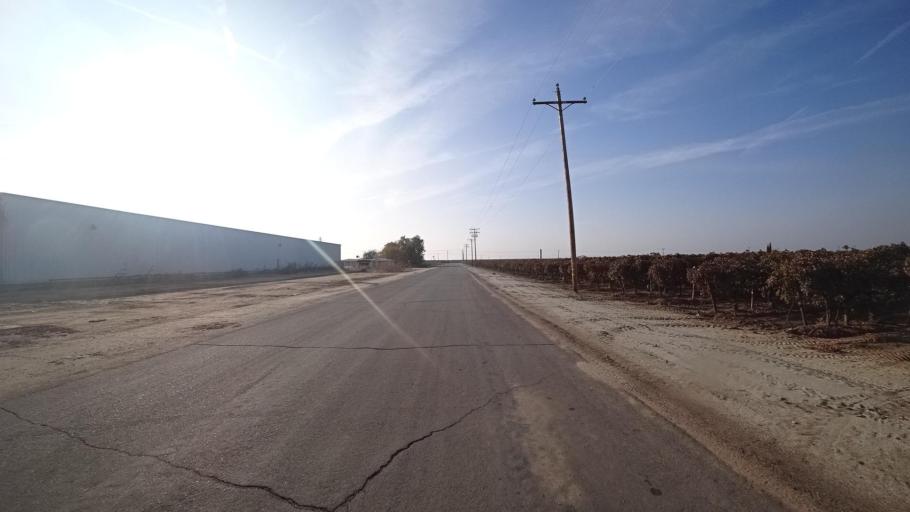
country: US
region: California
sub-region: Kern County
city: McFarland
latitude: 35.6776
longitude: -119.1871
